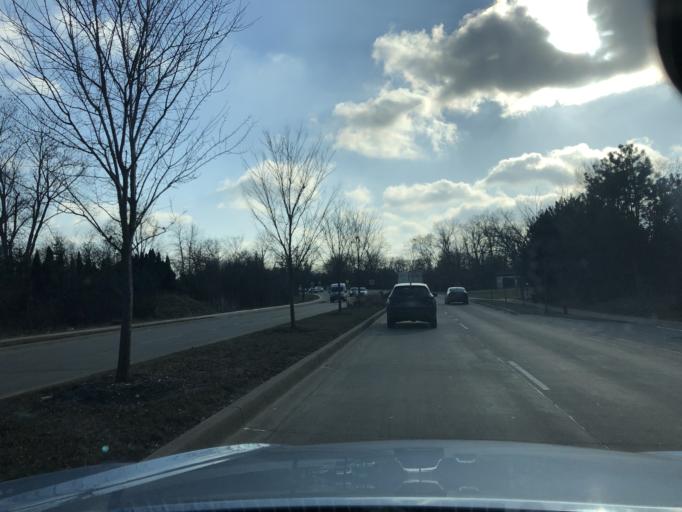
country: US
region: Illinois
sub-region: Cook County
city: Northfield
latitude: 42.1031
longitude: -87.7841
